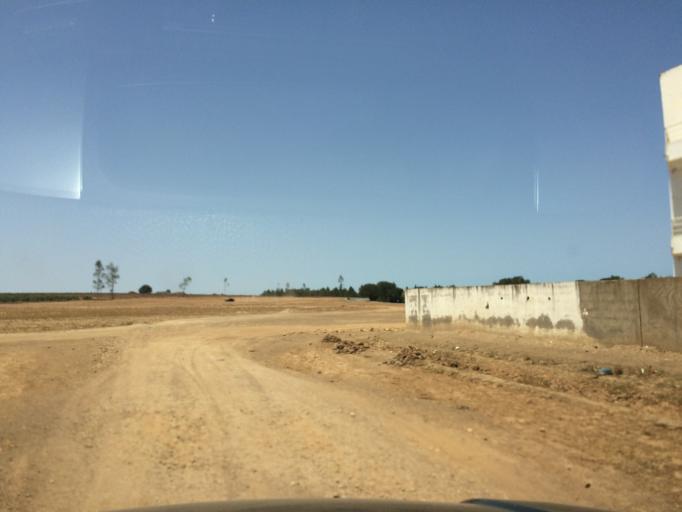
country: MA
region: Chaouia-Ouardigha
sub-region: Benslimane
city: Mellila
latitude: 33.5649
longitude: -6.8998
